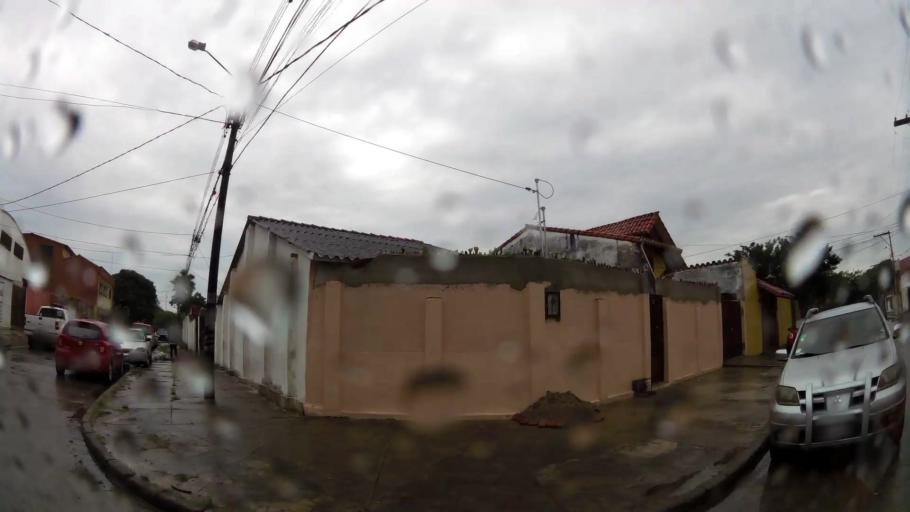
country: BO
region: Santa Cruz
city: Santa Cruz de la Sierra
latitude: -17.8046
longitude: -63.1744
